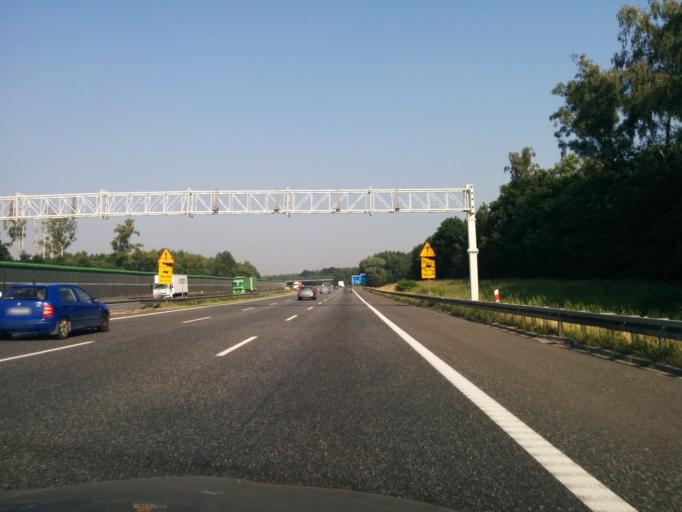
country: PL
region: Silesian Voivodeship
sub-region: Powiat gliwicki
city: Paniowki
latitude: 50.2655
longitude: 18.7796
